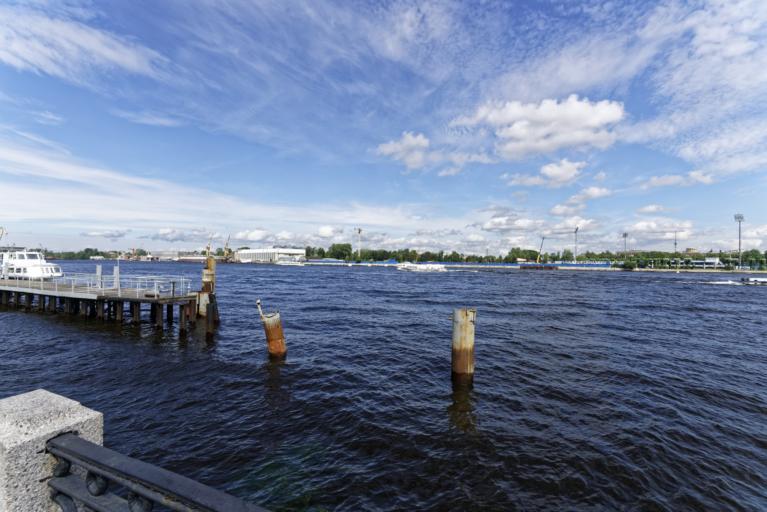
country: RU
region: St.-Petersburg
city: Vasyl'evsky Ostrov
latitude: 59.9498
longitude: 30.2775
